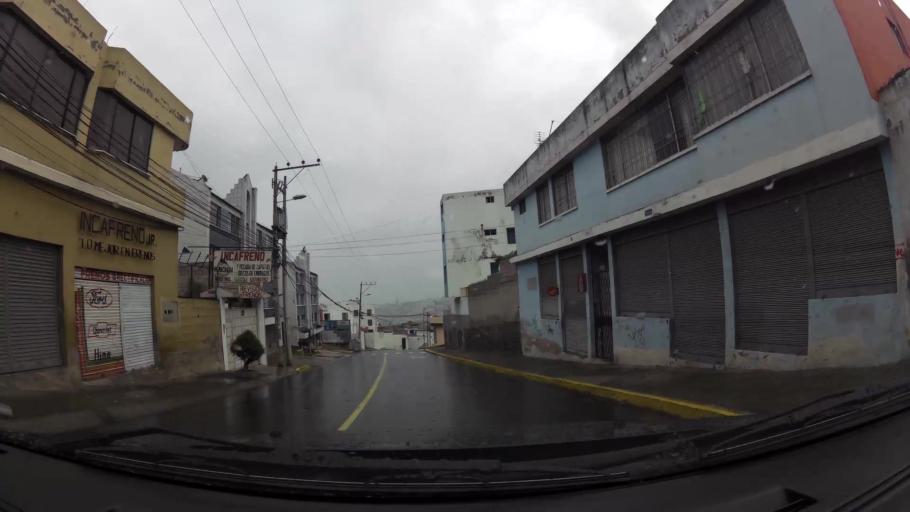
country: EC
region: Pichincha
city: Quito
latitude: -0.1204
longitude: -78.5045
